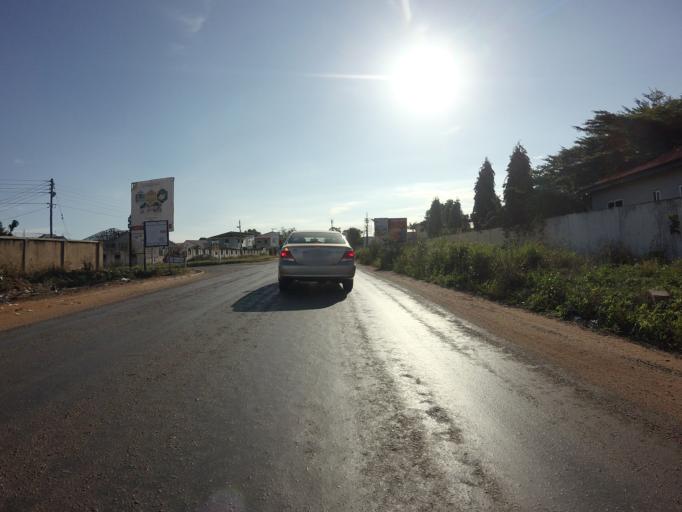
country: GH
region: Greater Accra
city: Nungua
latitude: 5.6492
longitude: -0.0743
